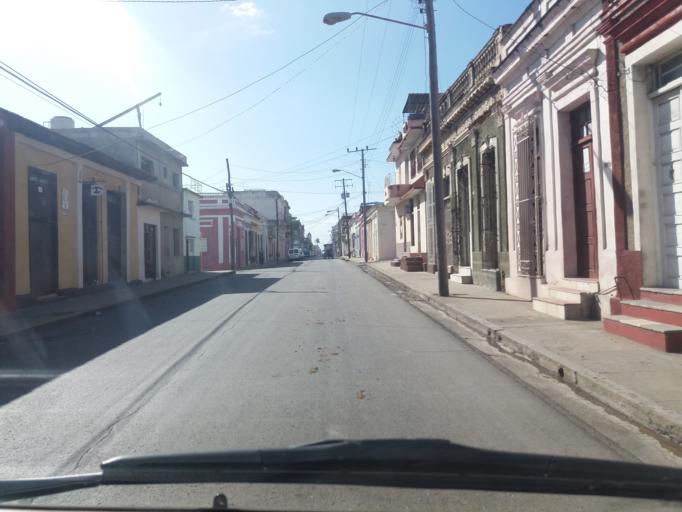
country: CU
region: Cienfuegos
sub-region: Municipio de Cienfuegos
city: Cienfuegos
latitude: 22.1456
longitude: -80.4450
